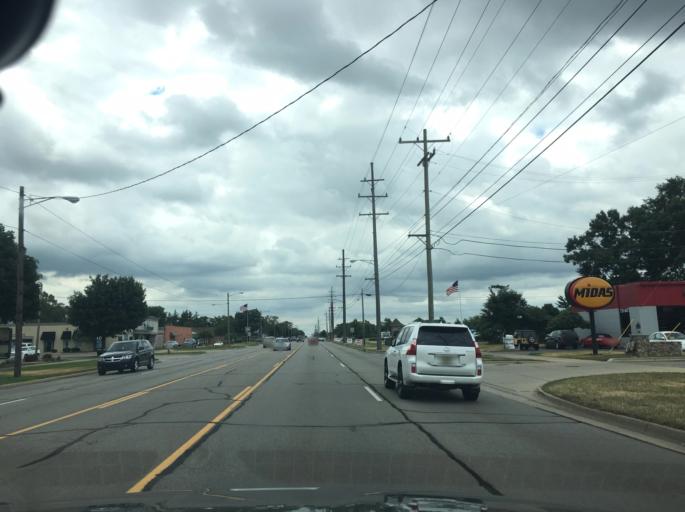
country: US
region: Michigan
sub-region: Macomb County
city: Shelby
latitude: 42.6630
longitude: -83.0337
